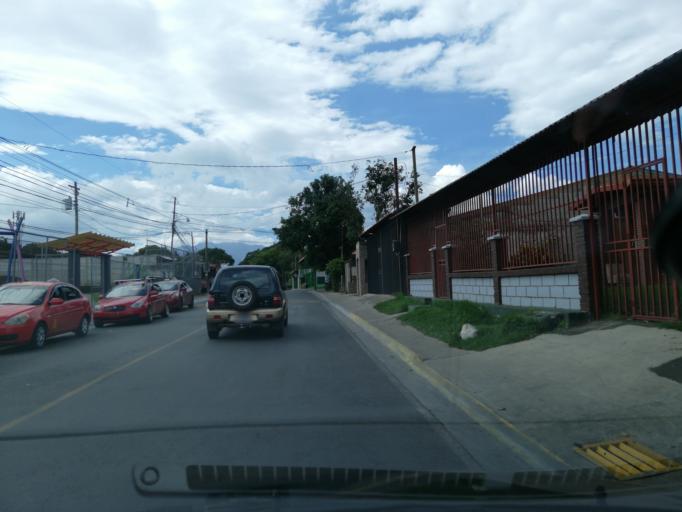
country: CR
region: Alajuela
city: Alajuela
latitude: 9.9866
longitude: -84.2442
